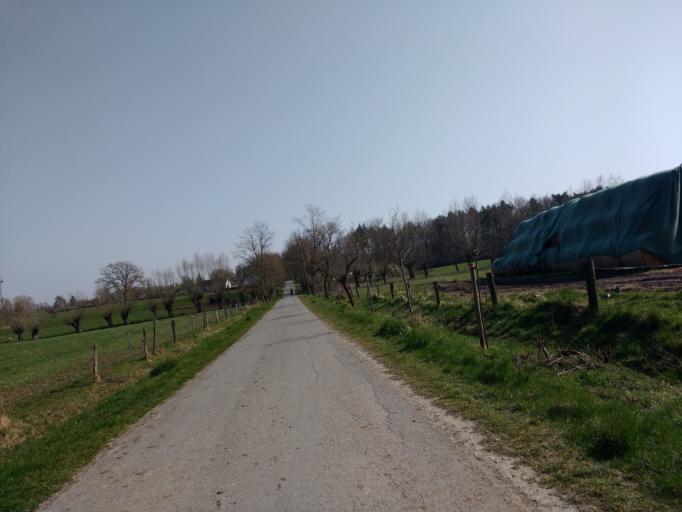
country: DE
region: North Rhine-Westphalia
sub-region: Regierungsbezirk Detmold
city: Salzkotten
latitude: 51.7234
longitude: 8.6365
